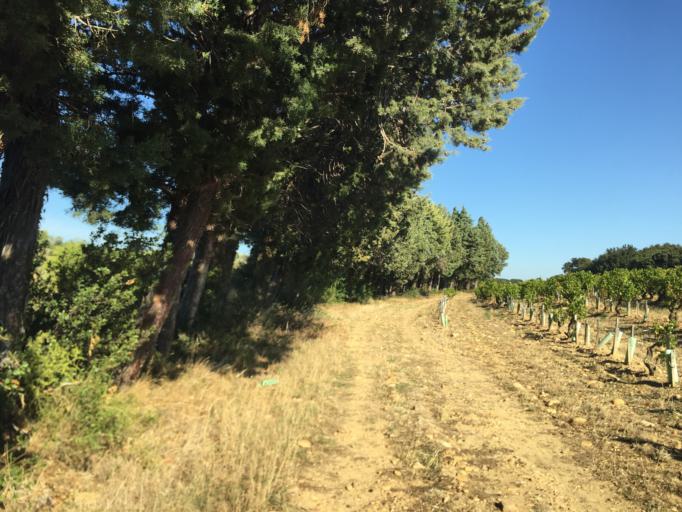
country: FR
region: Provence-Alpes-Cote d'Azur
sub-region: Departement du Vaucluse
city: Chateauneuf-du-Pape
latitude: 44.0578
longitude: 4.8435
